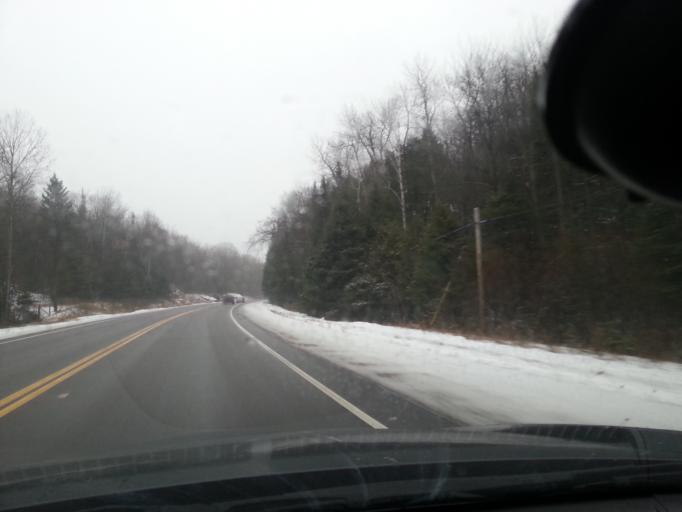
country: CA
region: Ontario
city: Perth
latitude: 44.7637
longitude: -76.7641
